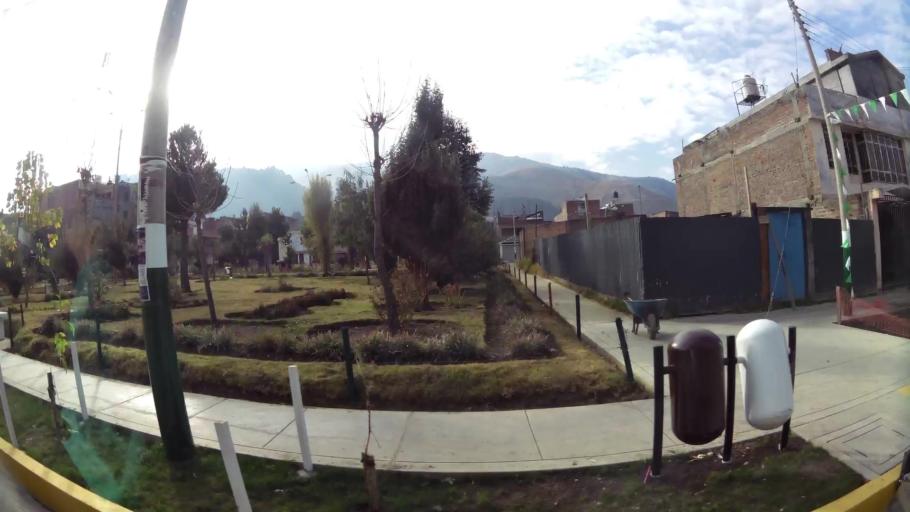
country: PE
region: Junin
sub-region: Provincia de Huancayo
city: Huancayo
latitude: -12.0418
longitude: -75.1927
